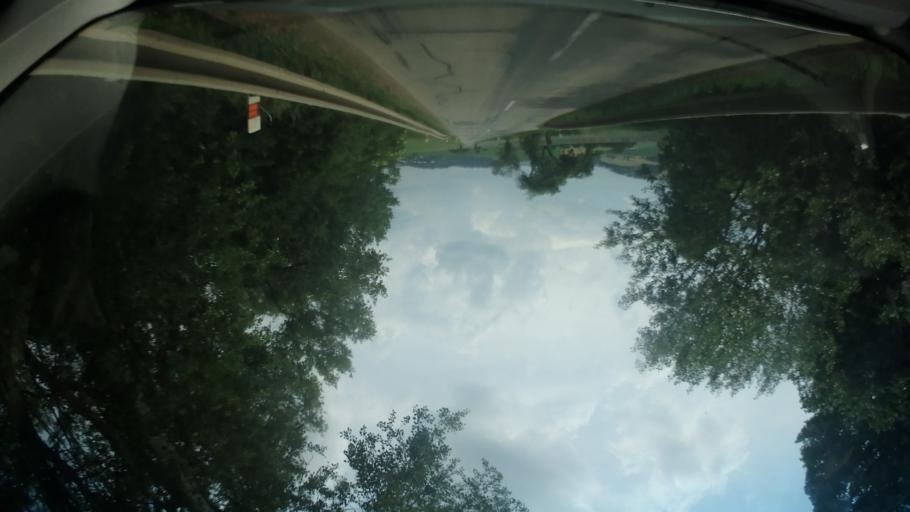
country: CZ
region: South Moravian
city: Lysice
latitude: 49.4409
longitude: 16.5583
